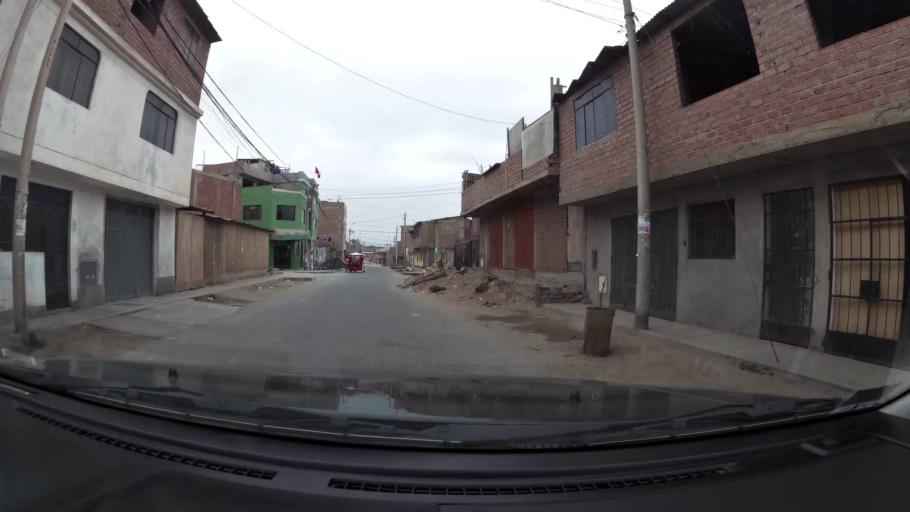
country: PE
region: Lima
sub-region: Lima
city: Surco
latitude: -12.1938
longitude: -76.9760
